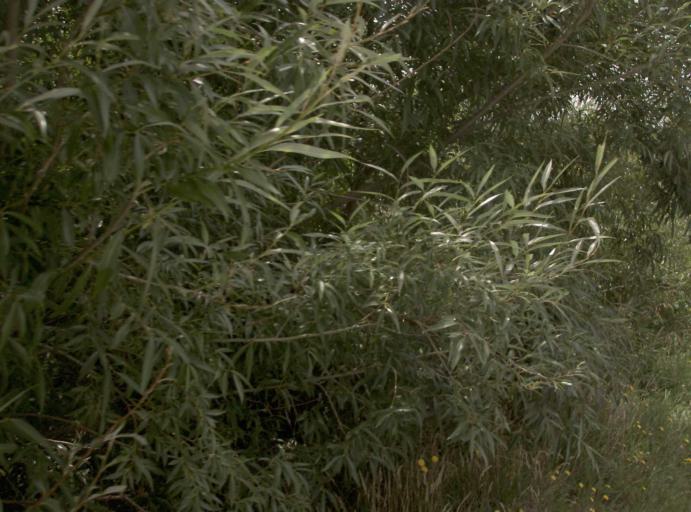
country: AU
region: Victoria
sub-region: Latrobe
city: Traralgon
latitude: -38.5028
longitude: 146.6677
